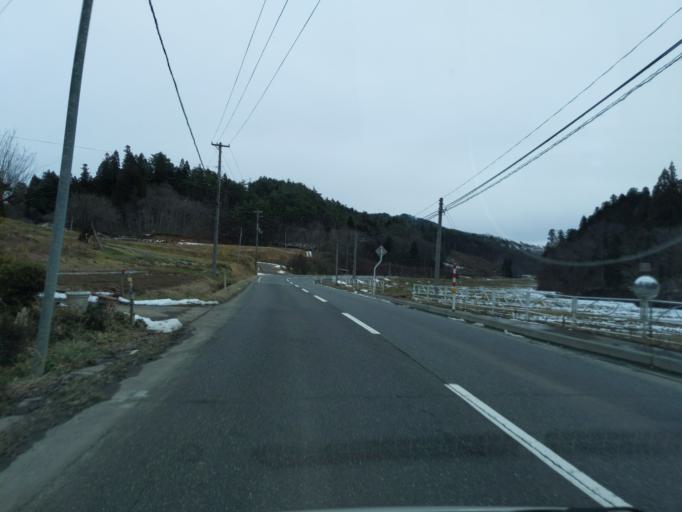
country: JP
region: Iwate
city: Mizusawa
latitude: 39.1518
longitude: 141.2406
